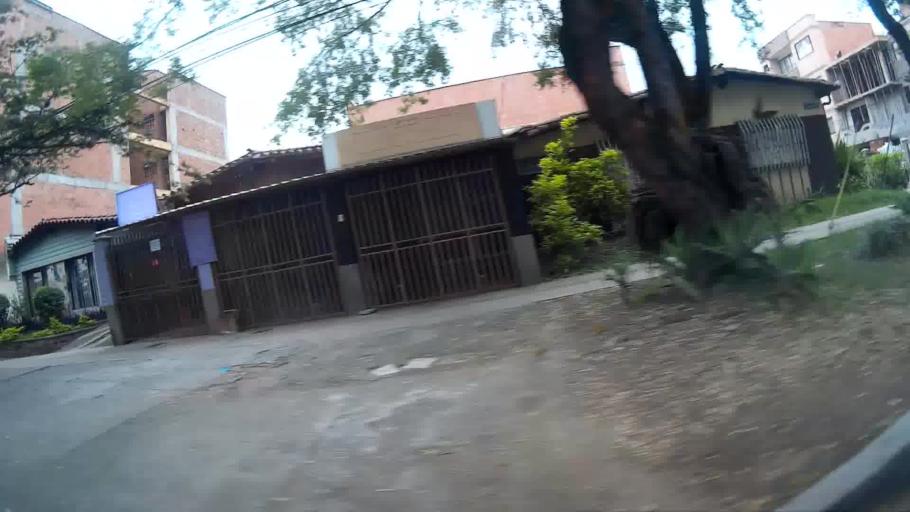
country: CO
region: Antioquia
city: Medellin
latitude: 6.2370
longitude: -75.5874
